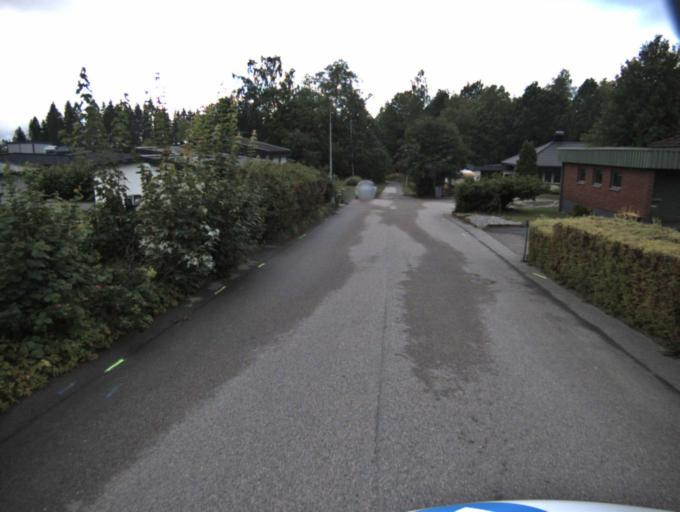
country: SE
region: Vaestra Goetaland
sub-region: Ulricehamns Kommun
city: Ulricehamn
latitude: 57.6764
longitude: 13.4617
